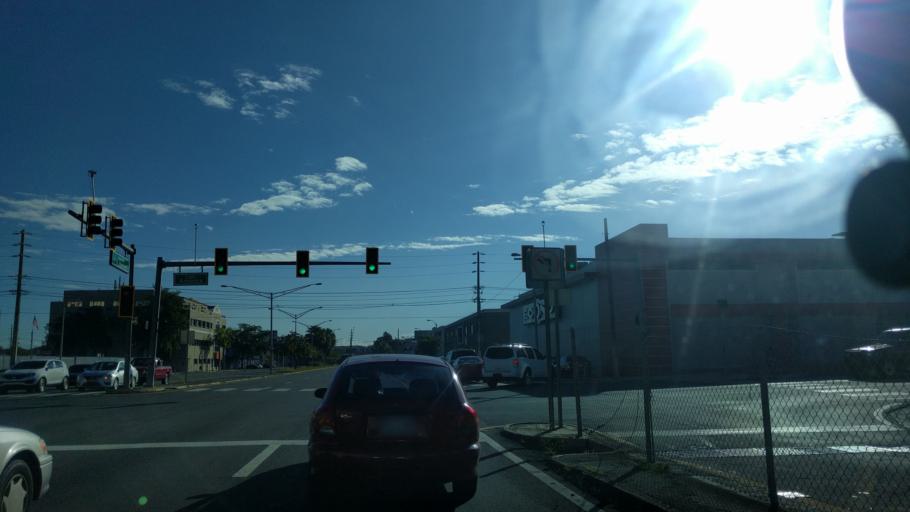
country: PR
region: San Juan
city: San Juan
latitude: 18.4251
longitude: -66.0509
